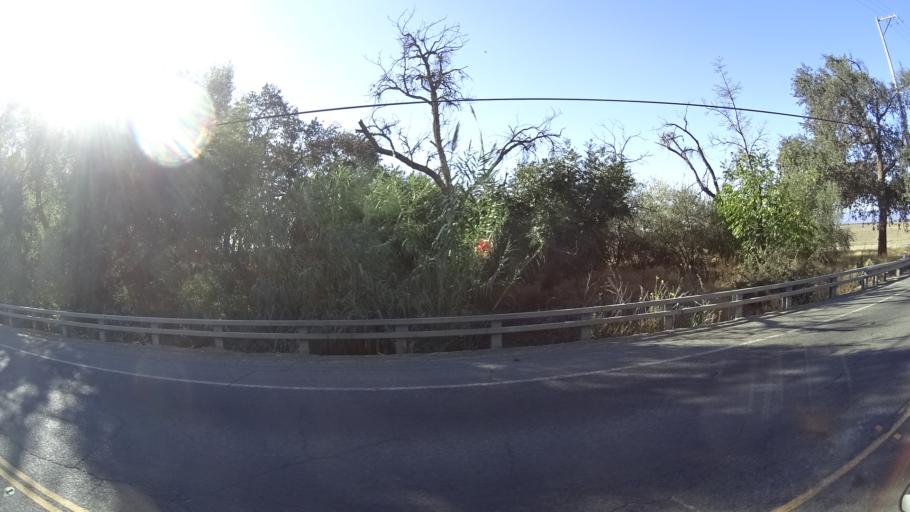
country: US
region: California
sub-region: Yolo County
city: Davis
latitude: 38.5616
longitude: -121.8564
